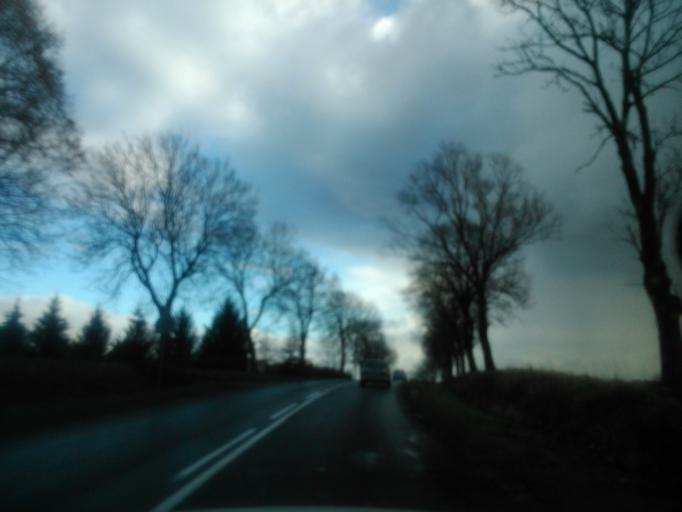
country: PL
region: Kujawsko-Pomorskie
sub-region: Powiat rypinski
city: Rypin
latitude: 53.0677
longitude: 19.3695
